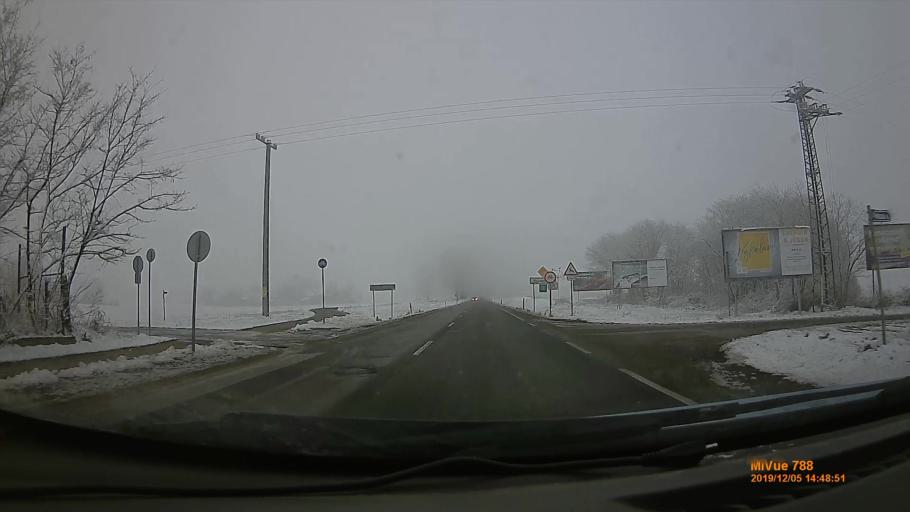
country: HU
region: Szabolcs-Szatmar-Bereg
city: Nyiregyhaza
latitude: 47.9791
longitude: 21.6841
